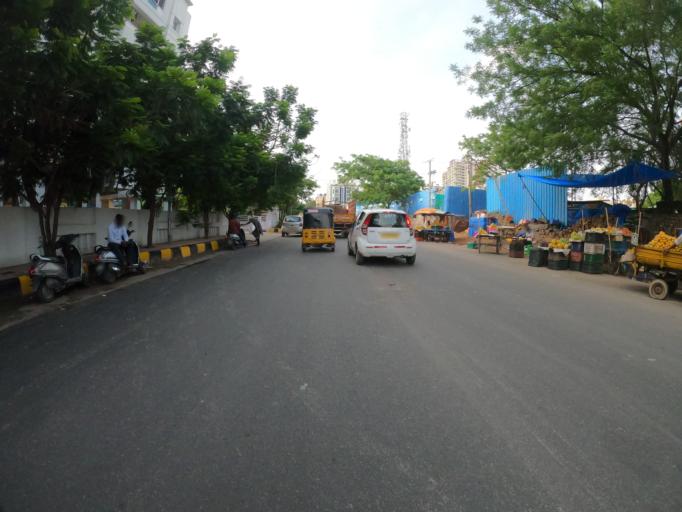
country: IN
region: Telangana
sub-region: Hyderabad
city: Hyderabad
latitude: 17.4097
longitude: 78.3948
